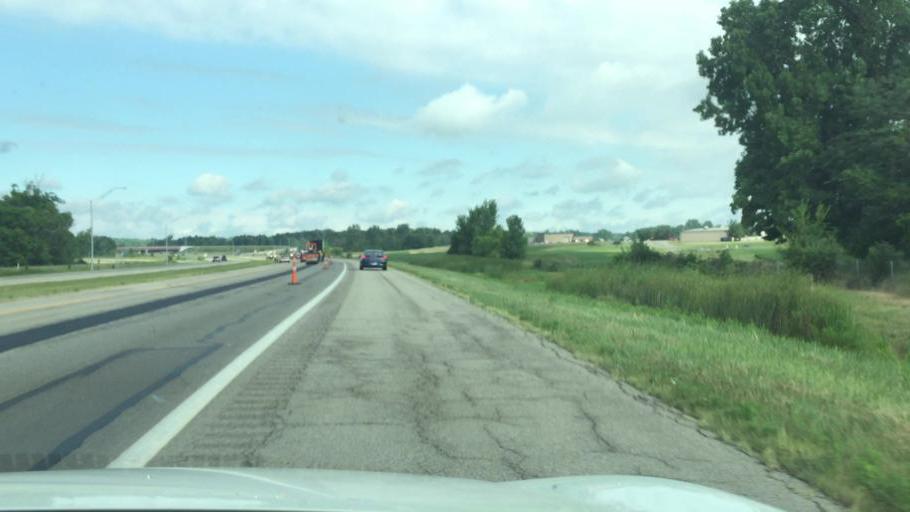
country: US
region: Ohio
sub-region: Champaign County
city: North Lewisburg
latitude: 40.3183
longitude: -83.5774
